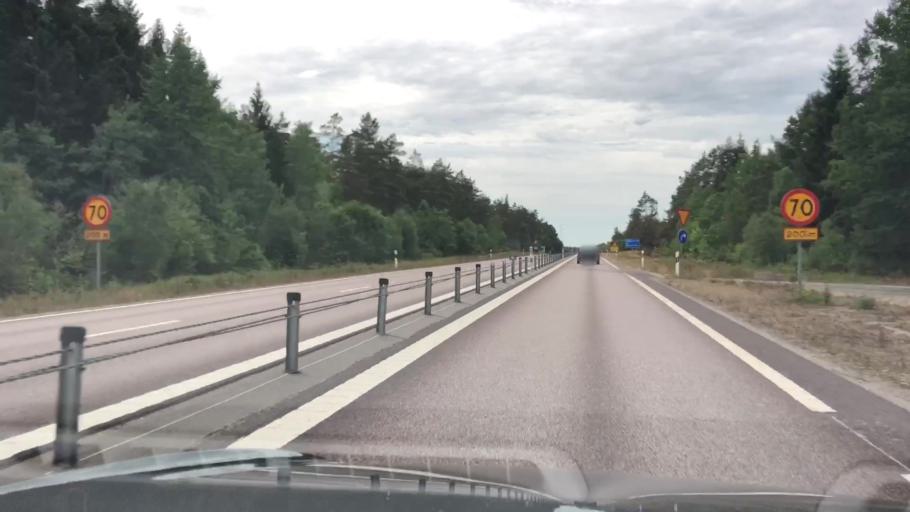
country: SE
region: Blekinge
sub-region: Karlskrona Kommun
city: Jaemjoe
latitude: 56.2038
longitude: 15.8623
